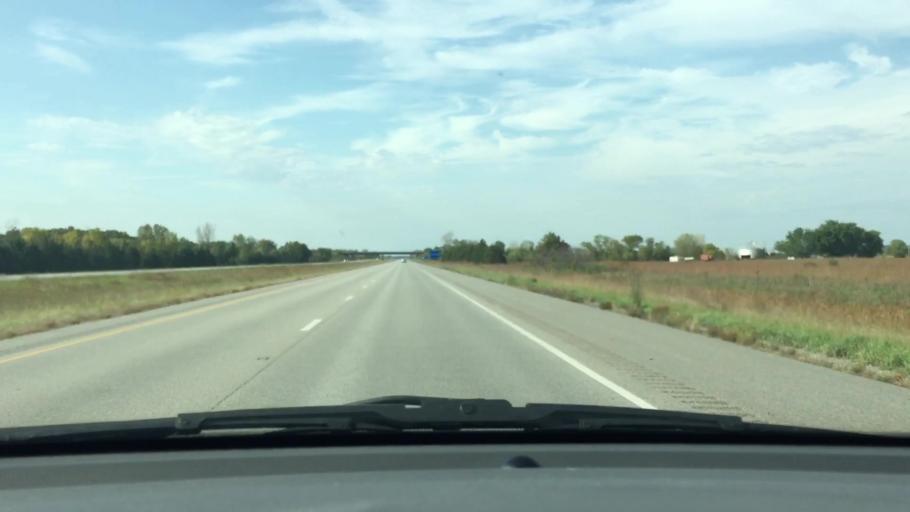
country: US
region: Illinois
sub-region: Rock Island County
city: Port Byron
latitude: 41.5761
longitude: -90.2168
